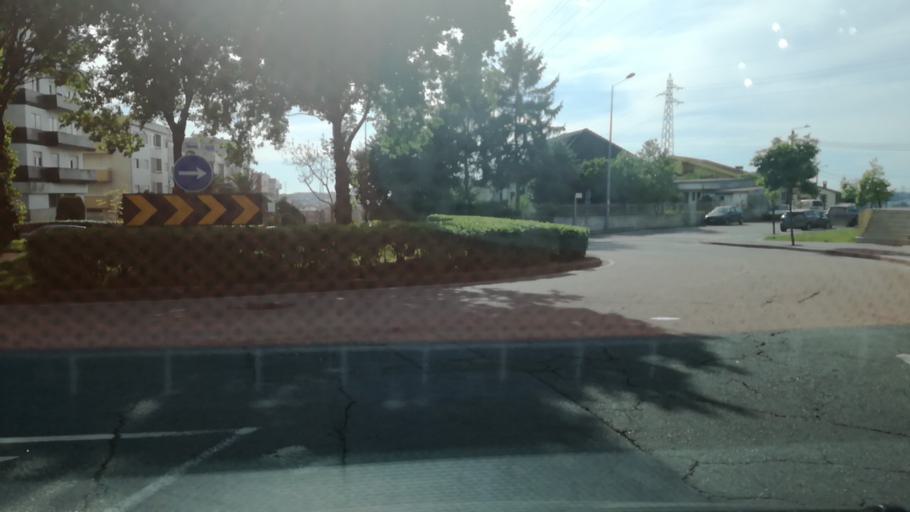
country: PT
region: Porto
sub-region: Maia
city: Nogueira
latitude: 41.2285
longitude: -8.5805
